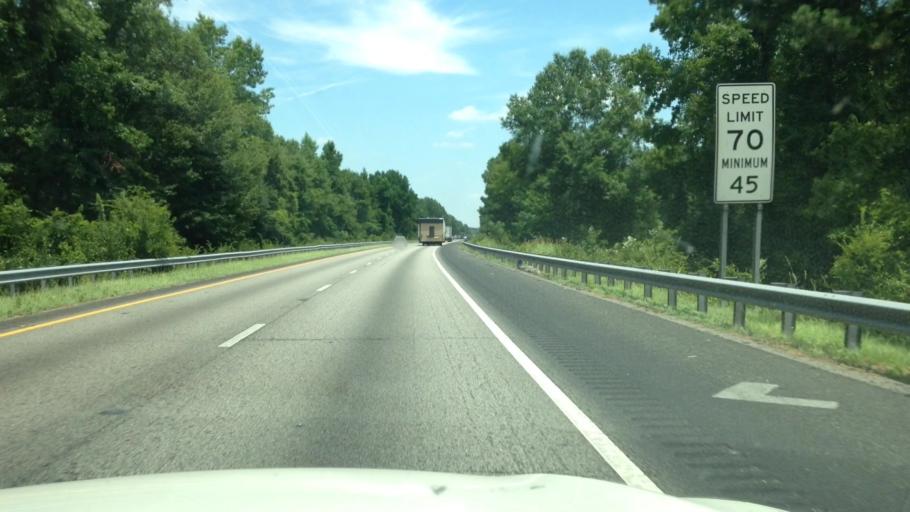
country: US
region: South Carolina
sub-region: Florence County
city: Florence
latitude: 34.2838
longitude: -79.6762
